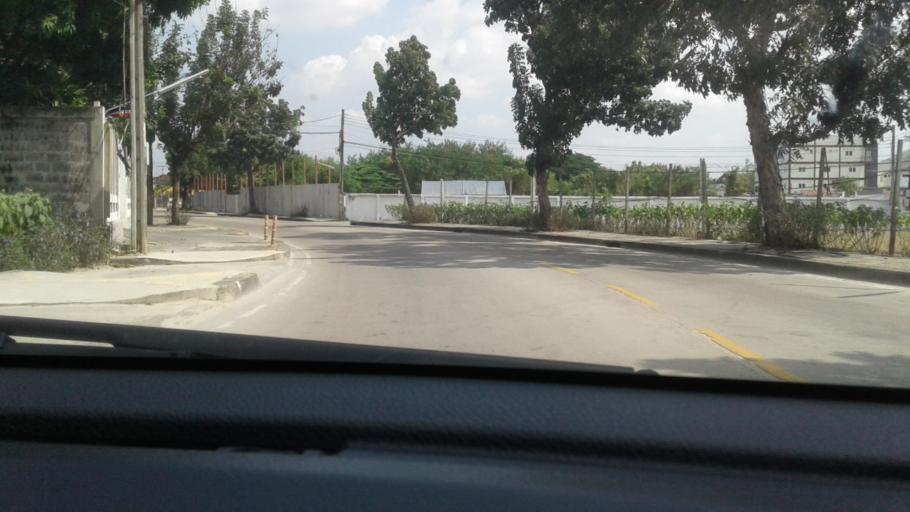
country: TH
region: Bangkok
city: Taling Chan
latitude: 13.7884
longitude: 100.4034
